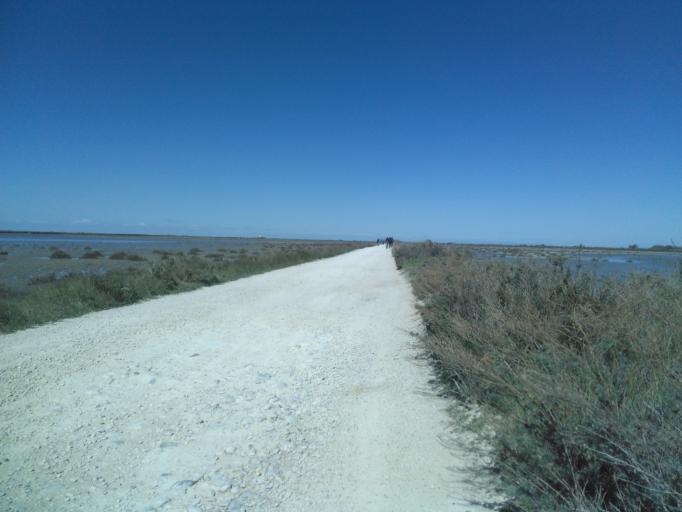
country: FR
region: Provence-Alpes-Cote d'Azur
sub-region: Departement des Bouches-du-Rhone
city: Saintes-Maries-de-la-Mer
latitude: 43.4482
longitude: 4.5986
